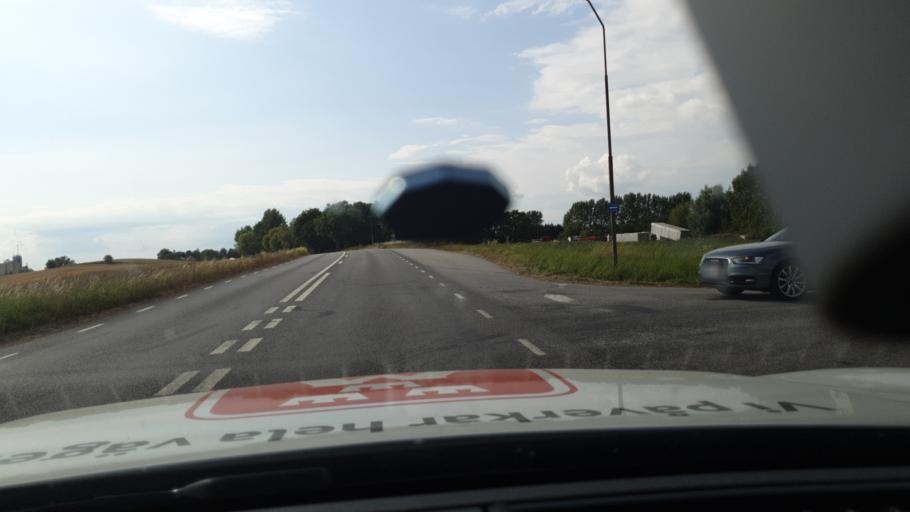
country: SE
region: Skane
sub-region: Svedala Kommun
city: Svedala
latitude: 55.4538
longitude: 13.2299
